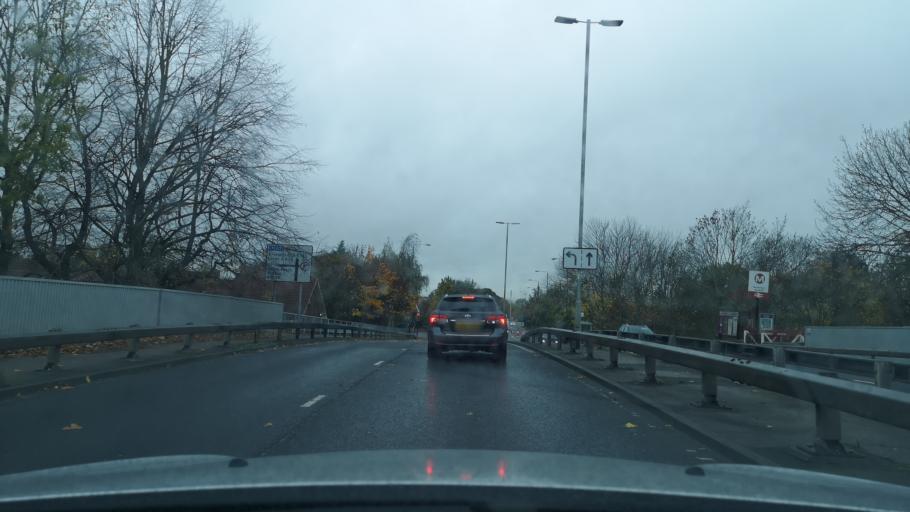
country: GB
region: England
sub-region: City and Borough of Wakefield
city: Pontefract
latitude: 53.6936
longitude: -1.3195
